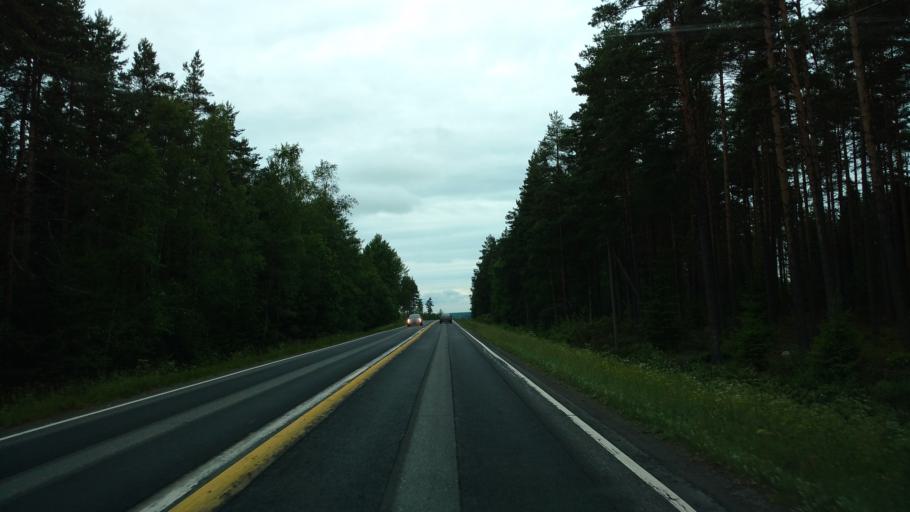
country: FI
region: Varsinais-Suomi
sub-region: Salo
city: Halikko
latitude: 60.4607
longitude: 23.0208
